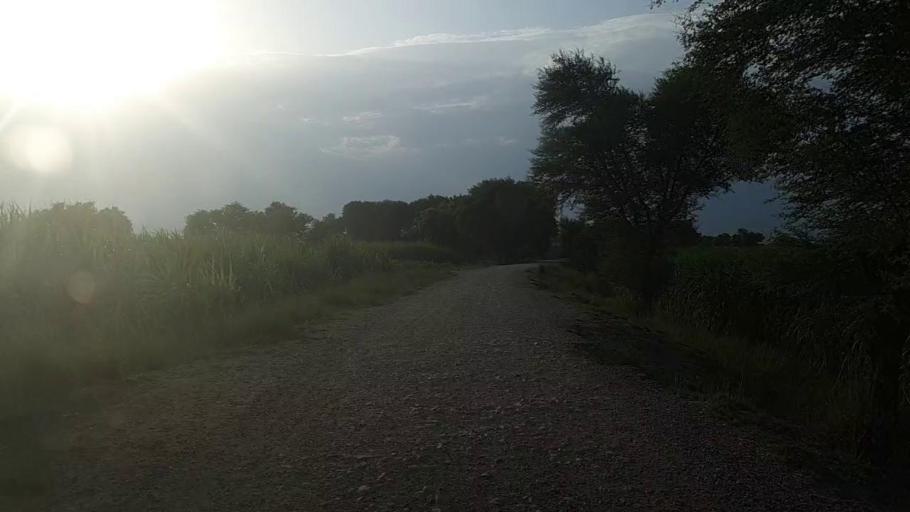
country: PK
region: Sindh
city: Ubauro
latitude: 28.3699
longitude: 69.7985
